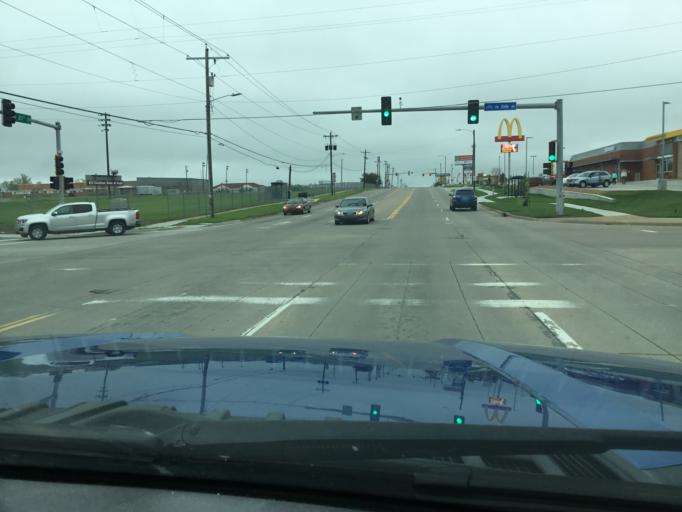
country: US
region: Kansas
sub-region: Shawnee County
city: Topeka
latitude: 39.0292
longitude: -95.7509
